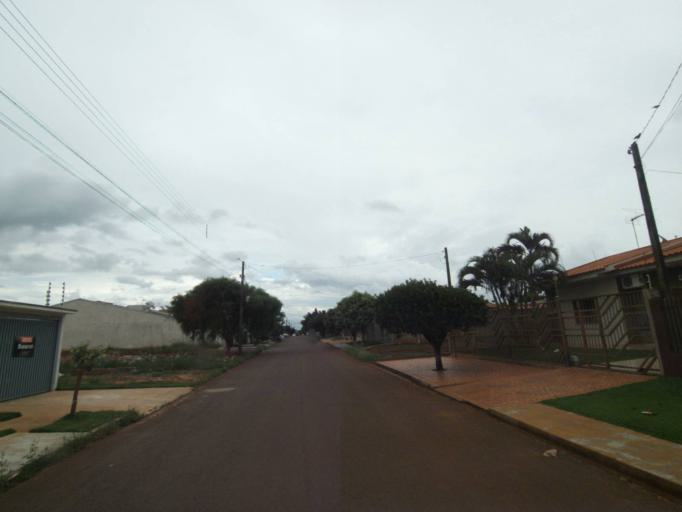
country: BR
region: Parana
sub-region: Campo Mourao
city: Campo Mourao
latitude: -24.0259
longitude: -52.3583
